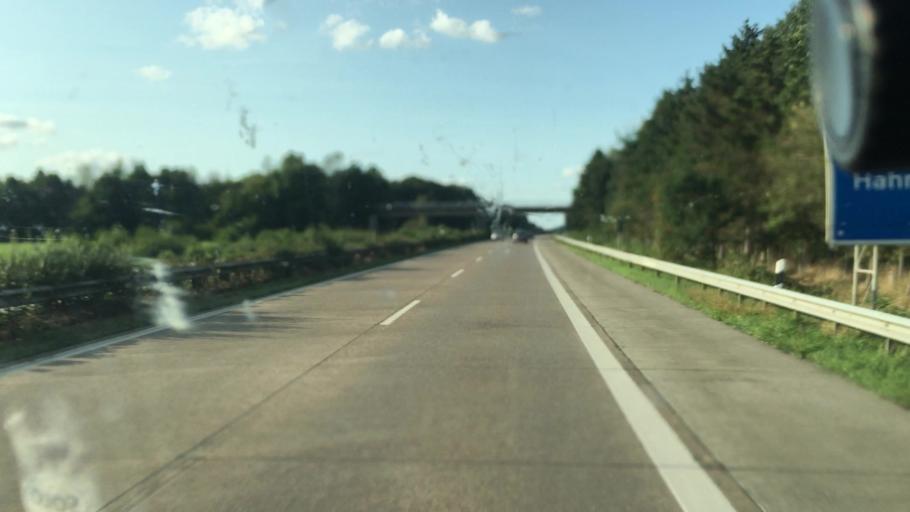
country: DE
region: Lower Saxony
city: Rastede
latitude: 53.2678
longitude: 8.1627
